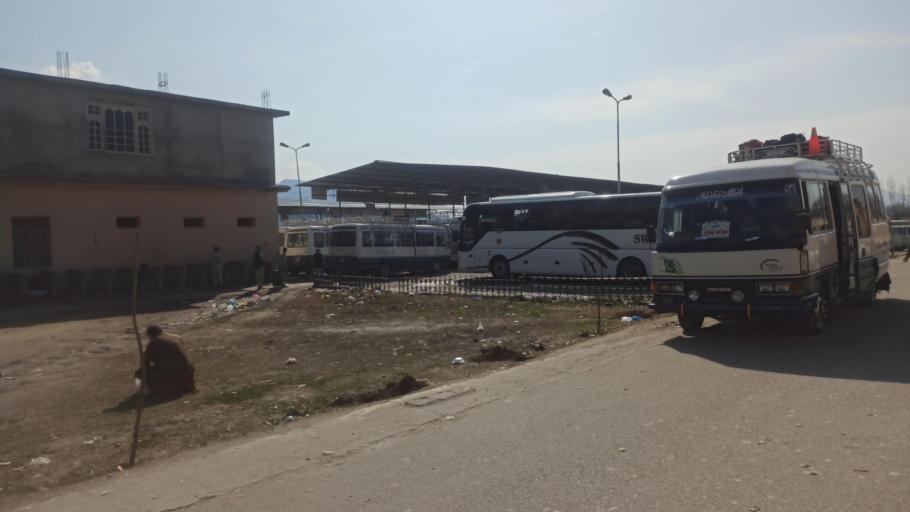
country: PK
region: Khyber Pakhtunkhwa
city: Mingora
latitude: 34.7785
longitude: 72.3330
